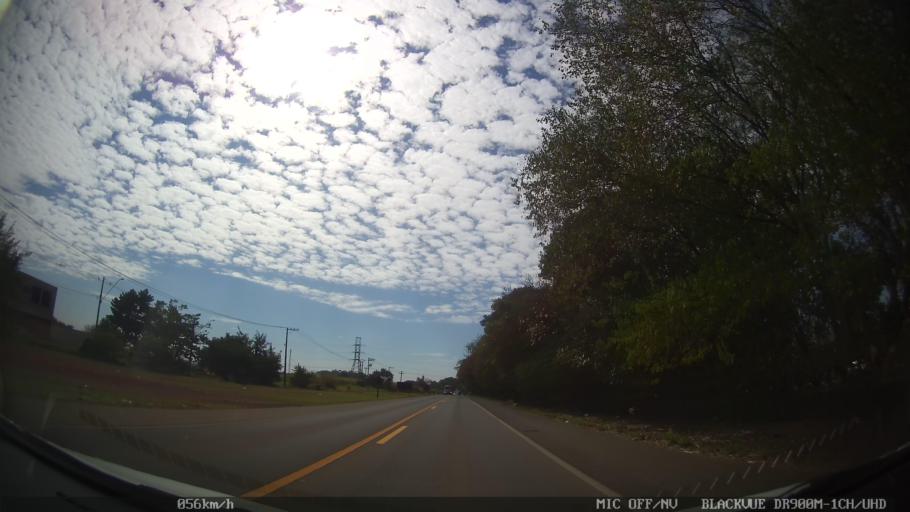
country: BR
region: Sao Paulo
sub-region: Santa Barbara D'Oeste
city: Santa Barbara d'Oeste
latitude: -22.7510
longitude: -47.4288
